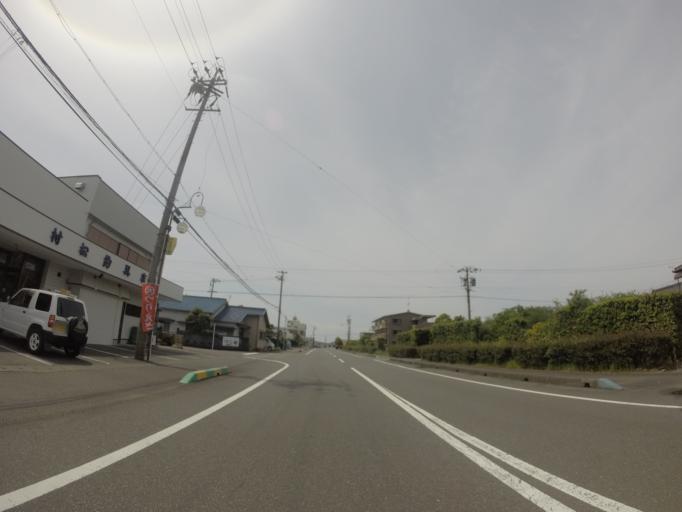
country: JP
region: Shizuoka
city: Yaizu
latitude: 34.7815
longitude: 138.2983
